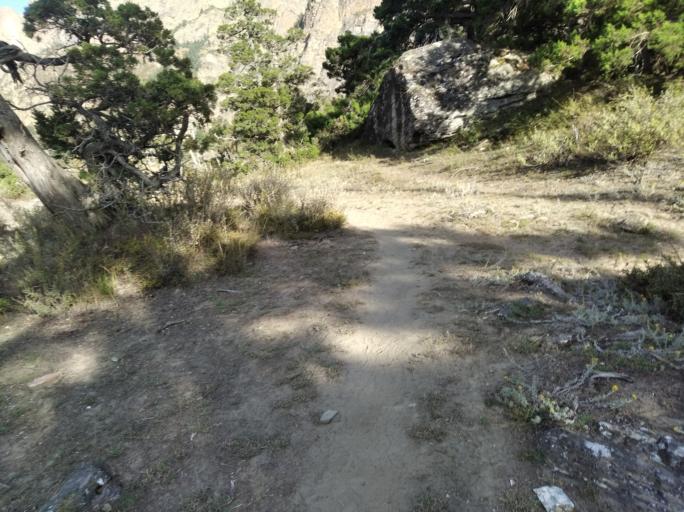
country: NP
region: Western Region
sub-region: Dhawalagiri Zone
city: Jomsom
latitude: 28.8761
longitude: 83.1513
